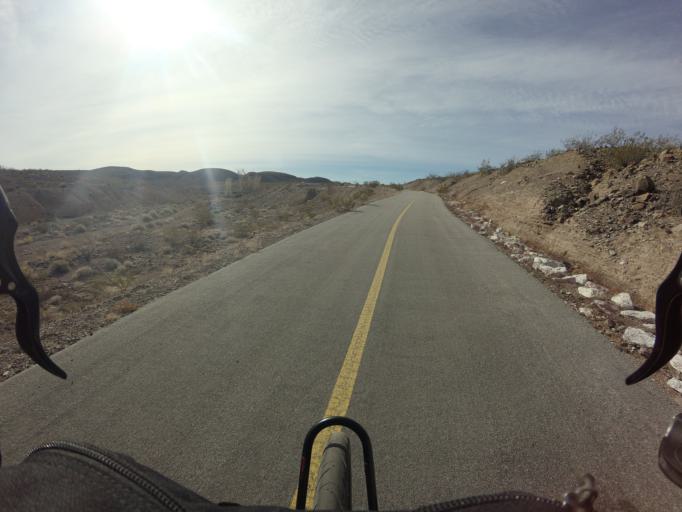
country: US
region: Nevada
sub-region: Clark County
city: Henderson
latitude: 36.1089
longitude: -114.8864
